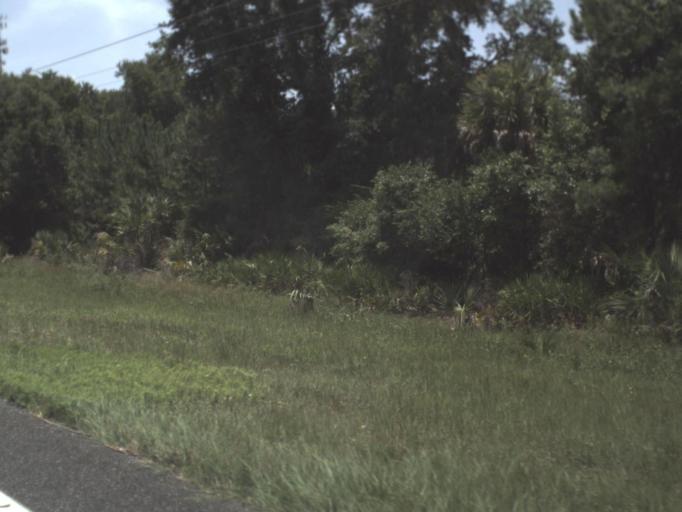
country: US
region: Florida
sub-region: Taylor County
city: Steinhatchee
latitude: 29.7819
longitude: -83.3284
